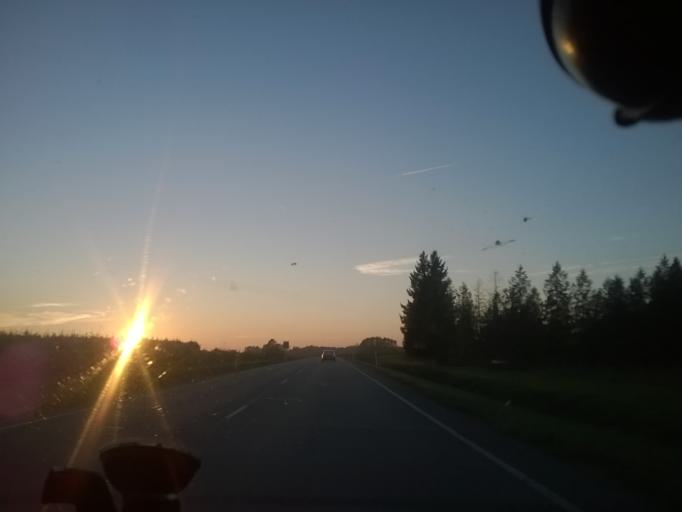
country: EE
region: Laeaene
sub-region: Ridala Parish
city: Uuemoisa
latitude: 58.9577
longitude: 23.8006
